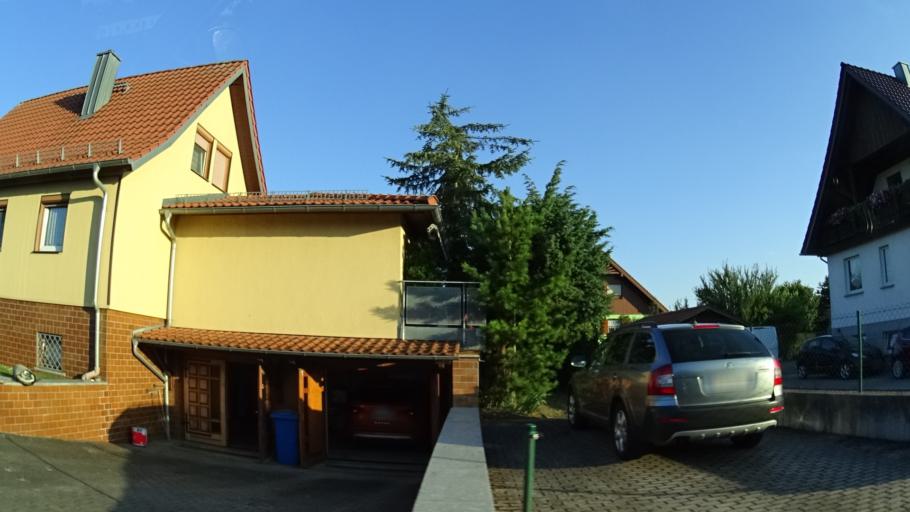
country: DE
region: Thuringia
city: Wolfershausen
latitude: 50.4542
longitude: 10.4349
